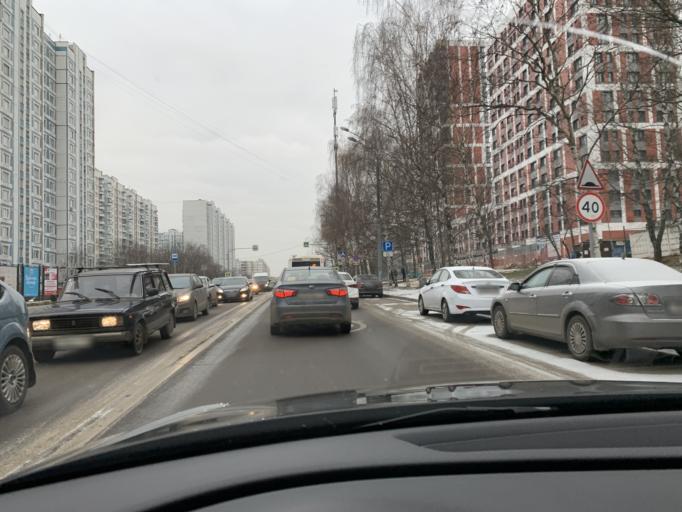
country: RU
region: Moscow
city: Zapadnoye Degunino
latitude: 55.8773
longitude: 37.5399
